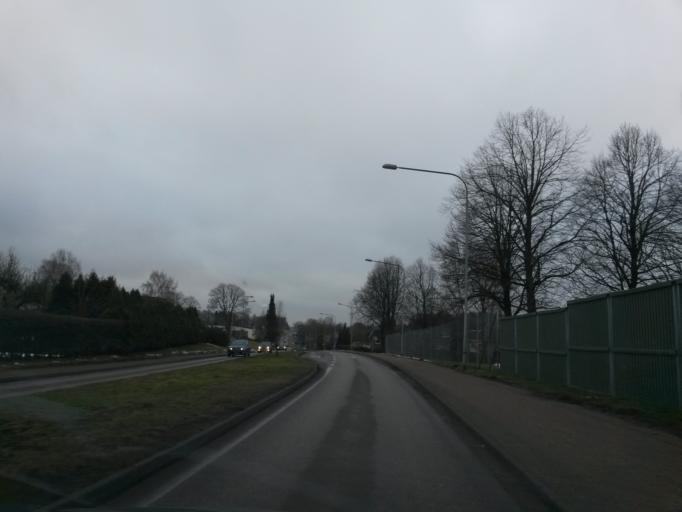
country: SE
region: Vaestra Goetaland
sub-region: Marks Kommun
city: Kinna
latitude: 57.5029
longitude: 12.6754
